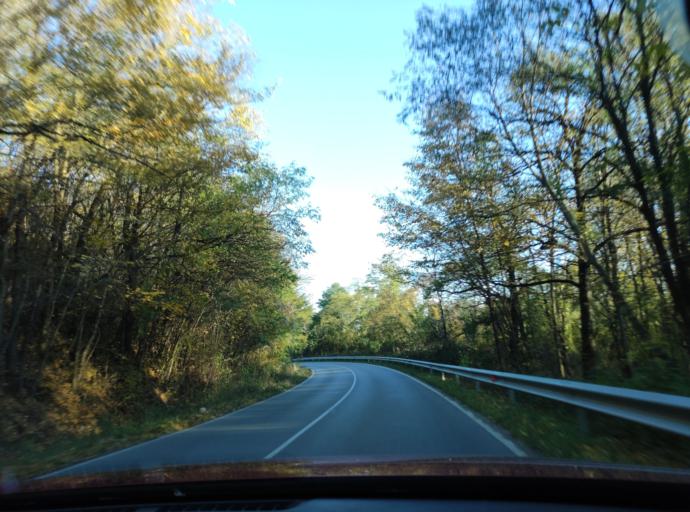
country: BG
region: Montana
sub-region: Obshtina Montana
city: Montana
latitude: 43.4069
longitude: 23.0529
